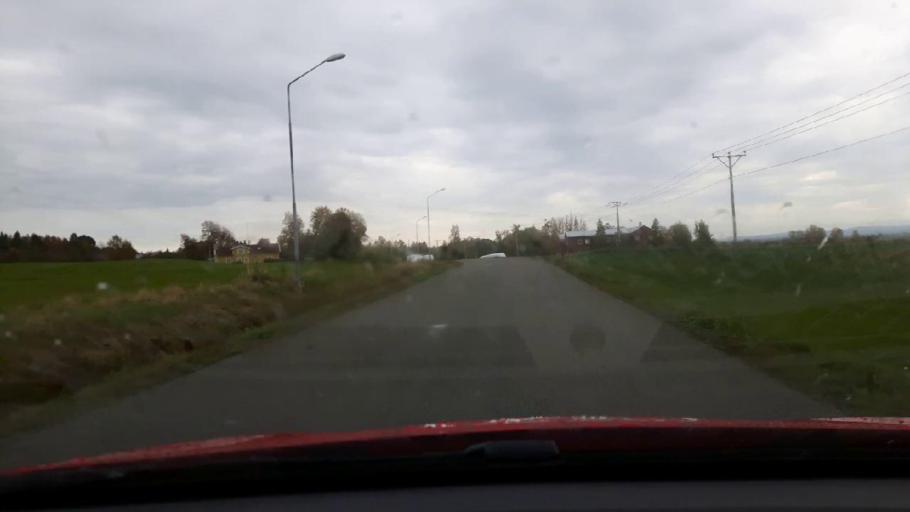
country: SE
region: Jaemtland
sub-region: Bergs Kommun
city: Hoverberg
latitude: 62.9426
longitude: 14.4974
